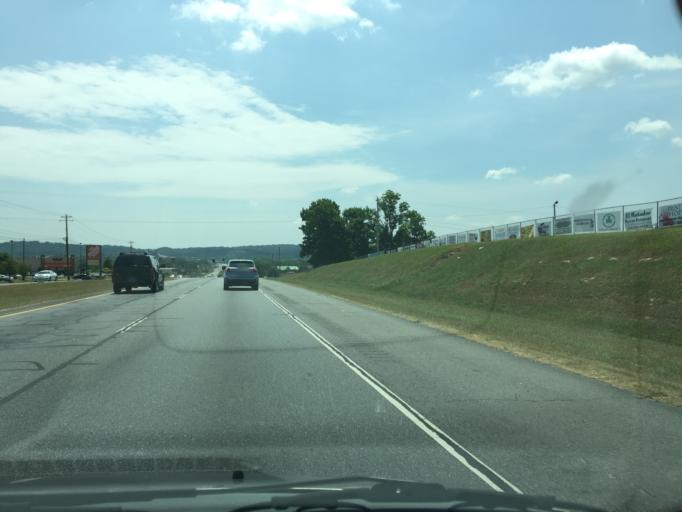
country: US
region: Georgia
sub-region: Catoosa County
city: Fort Oglethorpe
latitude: 34.9474
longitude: -85.2333
